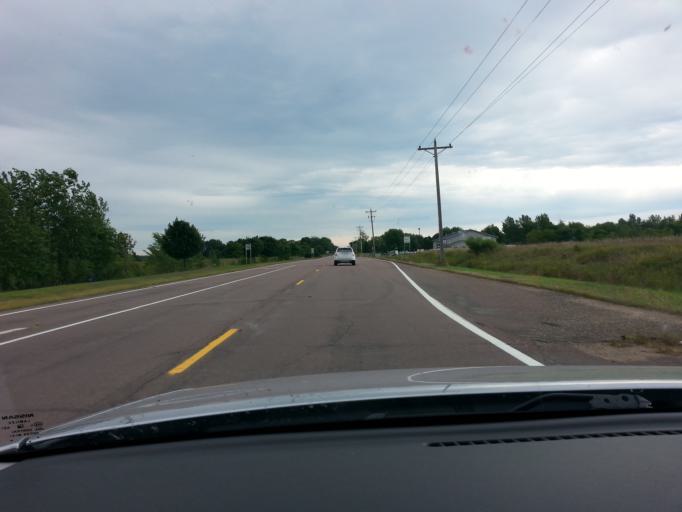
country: US
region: Minnesota
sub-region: Dakota County
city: Farmington
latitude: 44.6306
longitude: -93.1303
